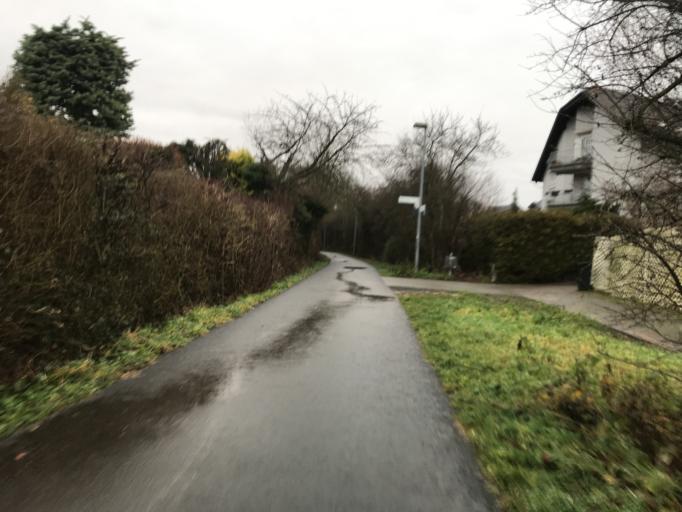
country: DE
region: Rheinland-Pfalz
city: Gau-Bischofsheim
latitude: 49.9060
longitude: 8.2791
